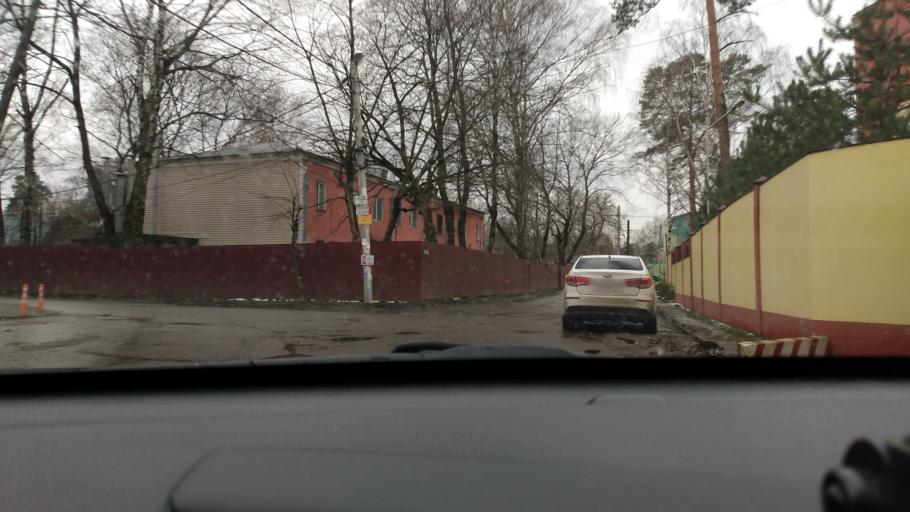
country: RU
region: Moskovskaya
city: Druzhba
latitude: 55.8965
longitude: 37.7438
